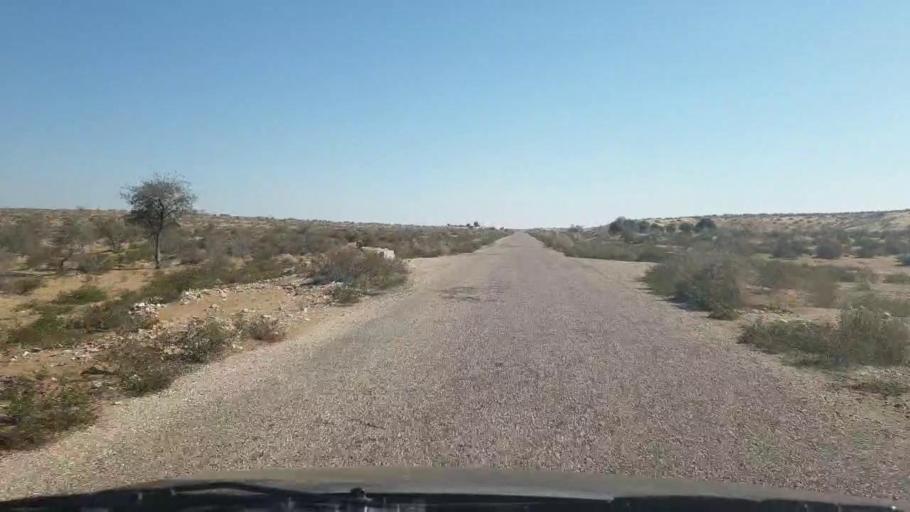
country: PK
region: Sindh
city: Bozdar
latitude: 27.0178
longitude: 68.7771
